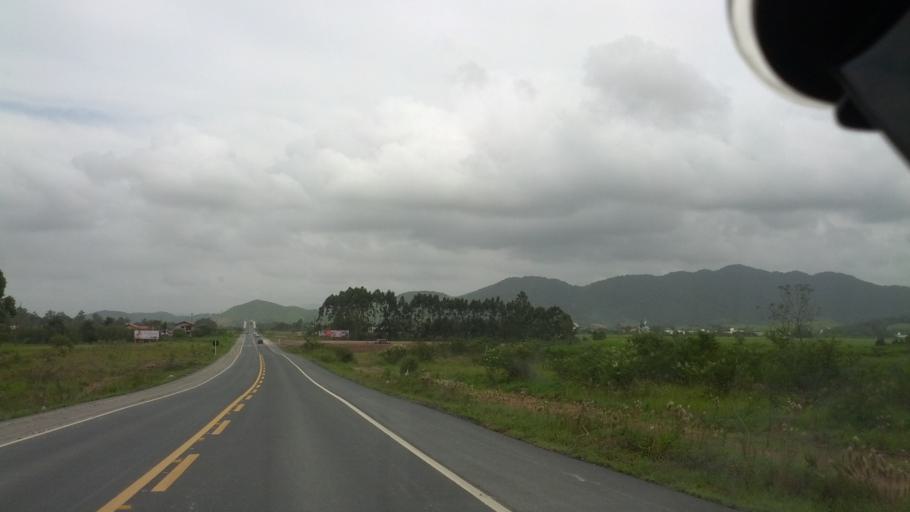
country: BR
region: Santa Catarina
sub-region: Gaspar
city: Gaspar
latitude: -26.8859
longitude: -48.8340
